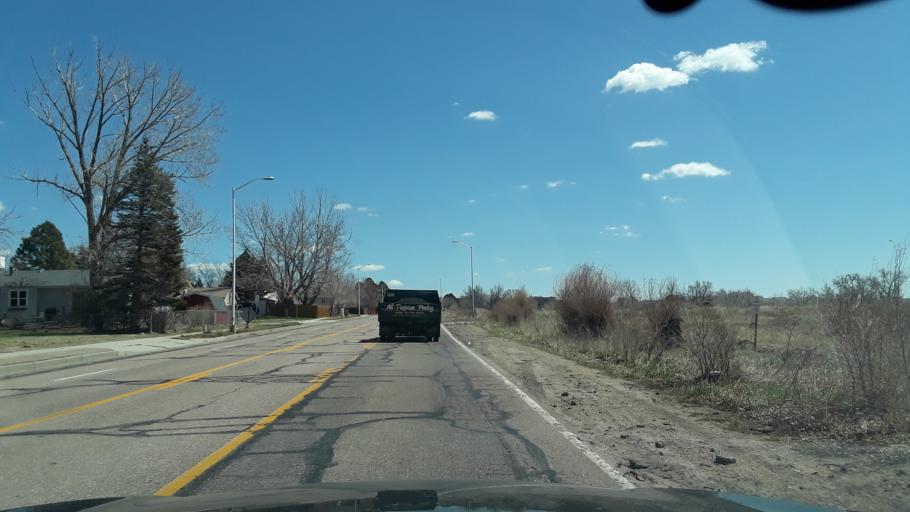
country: US
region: Colorado
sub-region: El Paso County
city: Cimarron Hills
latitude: 38.8466
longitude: -104.7288
